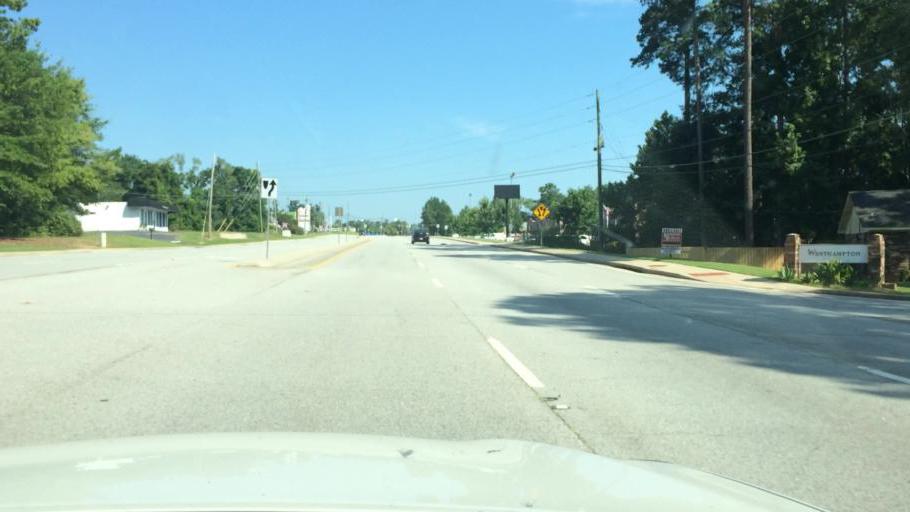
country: US
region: Georgia
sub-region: Columbia County
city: Martinez
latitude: 33.5251
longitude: -82.0697
